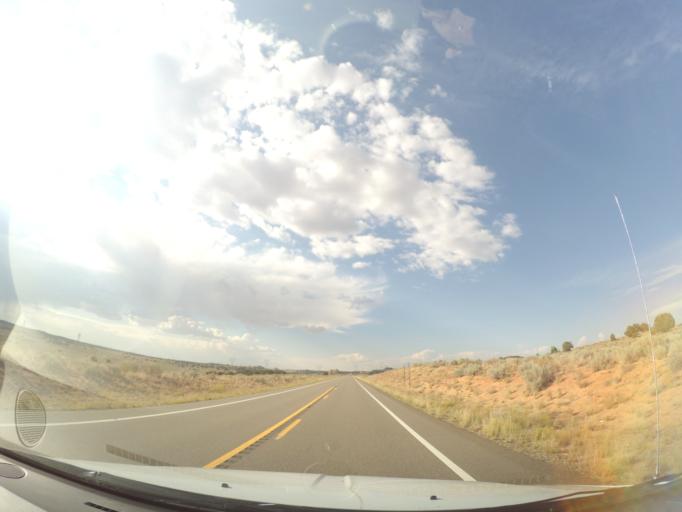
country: US
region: Arizona
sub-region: Coconino County
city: LeChee
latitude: 36.5951
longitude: -111.4255
